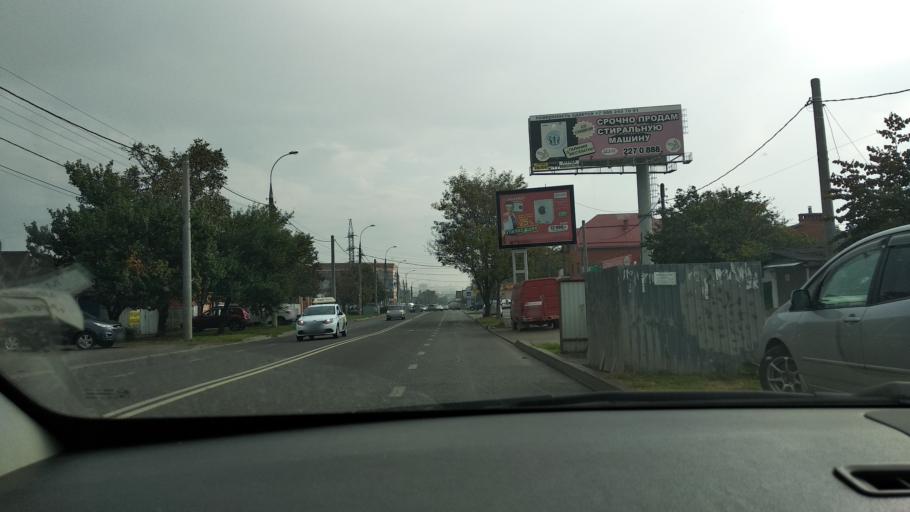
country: RU
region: Krasnodarskiy
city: Krasnodar
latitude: 45.0275
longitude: 39.0242
